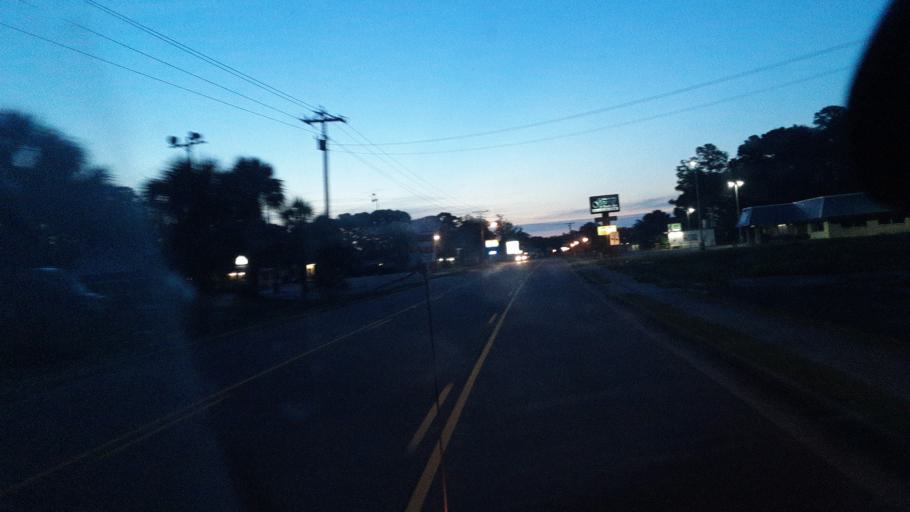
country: US
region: North Carolina
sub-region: Brunswick County
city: Calabash
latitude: 33.8908
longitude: -78.5738
